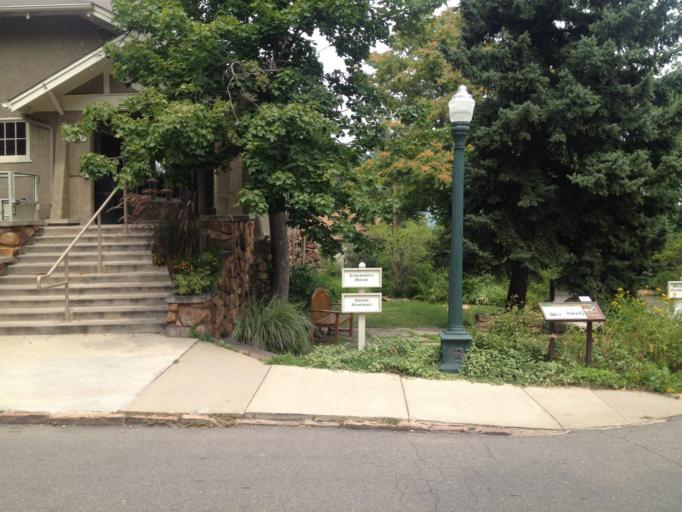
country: US
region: Colorado
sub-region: Boulder County
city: Boulder
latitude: 39.9977
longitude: -105.2812
